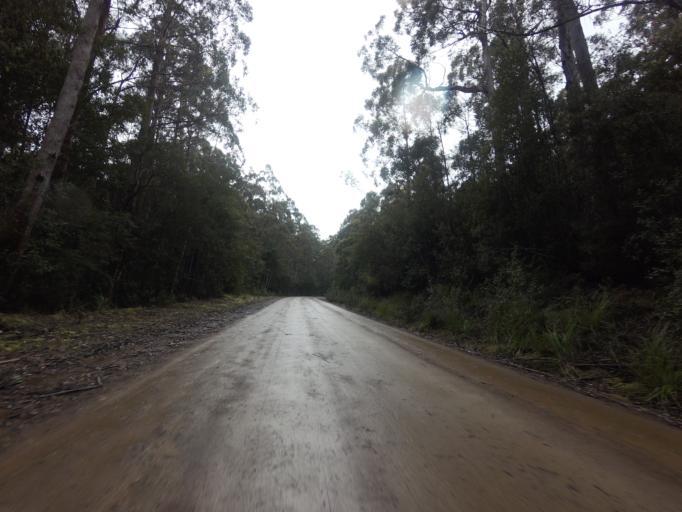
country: AU
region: Tasmania
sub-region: Huon Valley
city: Geeveston
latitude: -43.4930
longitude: 146.8829
